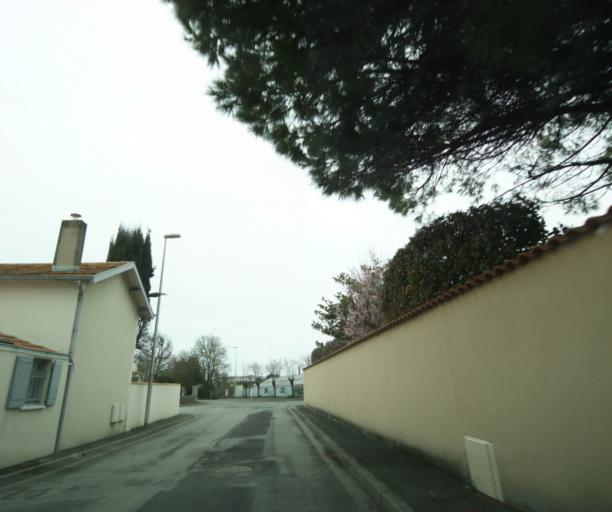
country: FR
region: Poitou-Charentes
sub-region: Departement de la Charente-Maritime
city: Lagord
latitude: 46.1824
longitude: -1.1417
